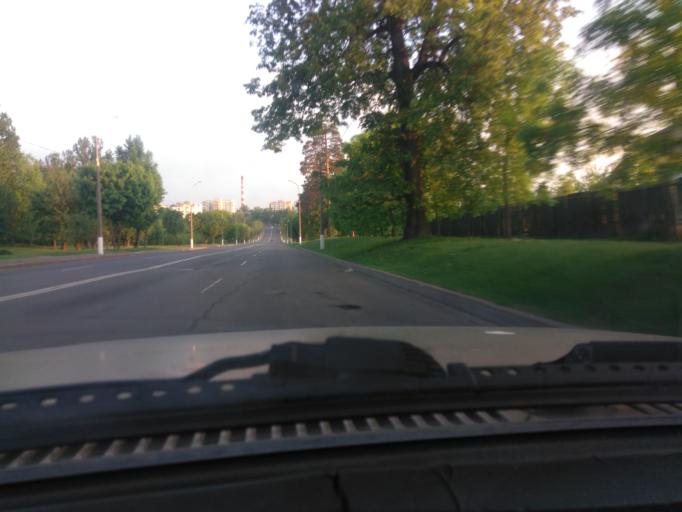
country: BY
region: Mogilev
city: Mahilyow
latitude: 53.9262
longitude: 30.3122
